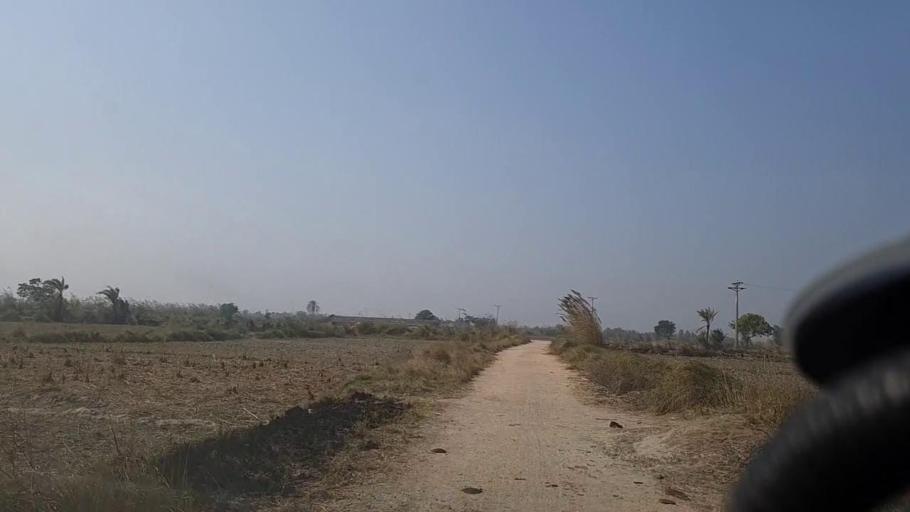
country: PK
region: Sindh
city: Thatta
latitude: 24.6617
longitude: 67.9250
